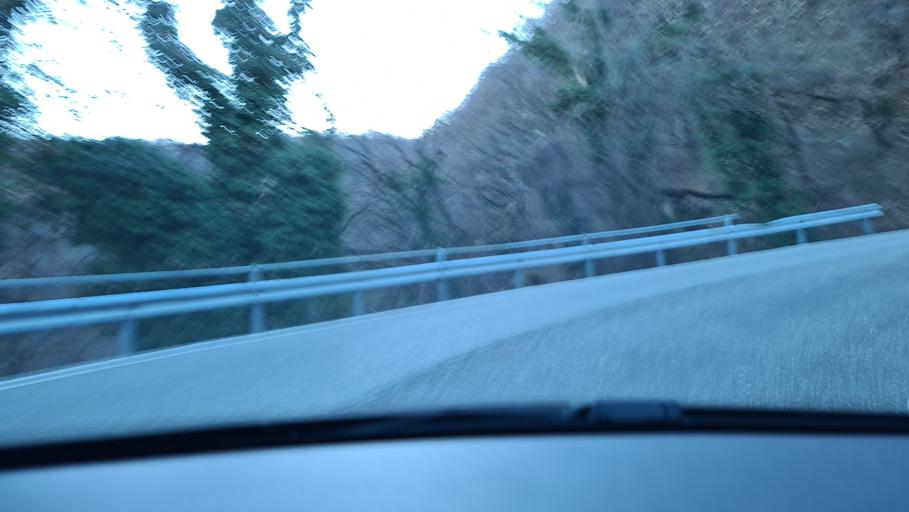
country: CH
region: Ticino
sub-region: Lugano District
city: Gravesano
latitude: 46.0421
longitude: 8.9088
